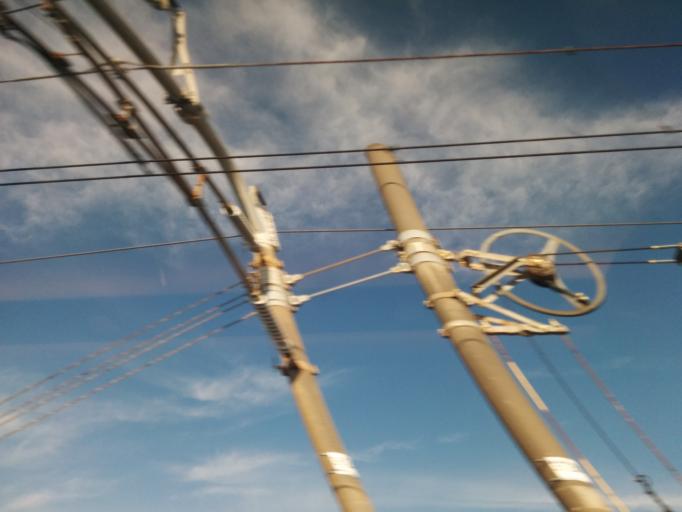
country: JP
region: Aichi
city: Sobue
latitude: 35.3081
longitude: 136.6951
